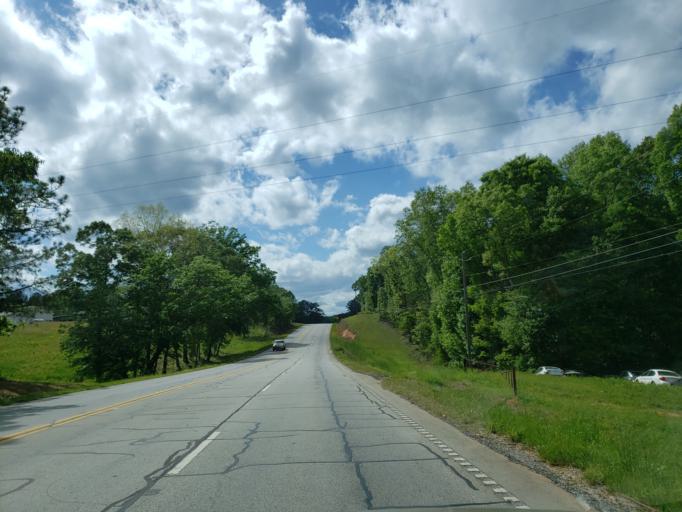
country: US
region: Georgia
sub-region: Haralson County
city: Tallapoosa
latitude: 33.7342
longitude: -85.2476
